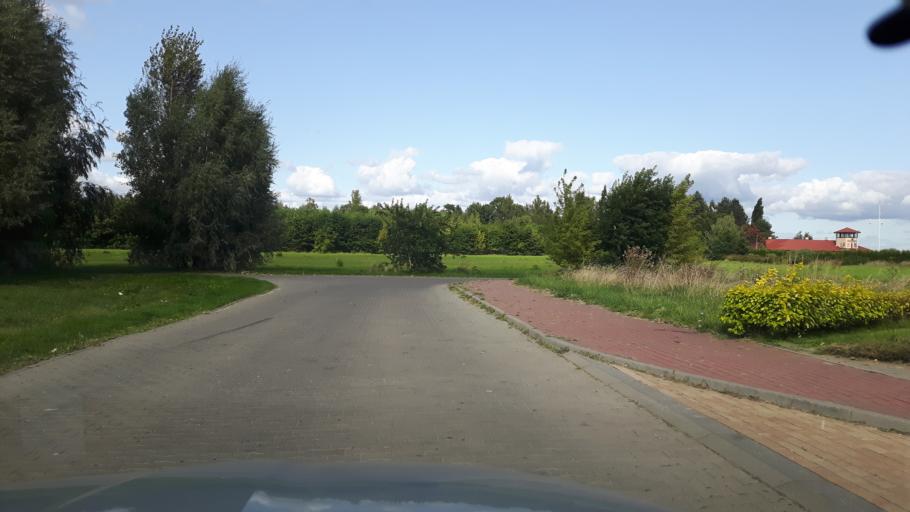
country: PL
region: Masovian Voivodeship
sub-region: Powiat legionowski
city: Nieporet
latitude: 52.4335
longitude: 21.0311
